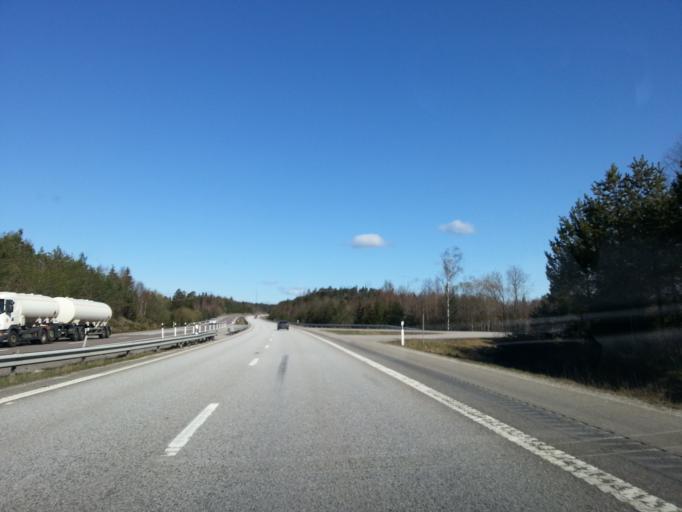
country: SE
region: Vaestra Goetaland
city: Svanesund
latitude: 58.1010
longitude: 11.8821
